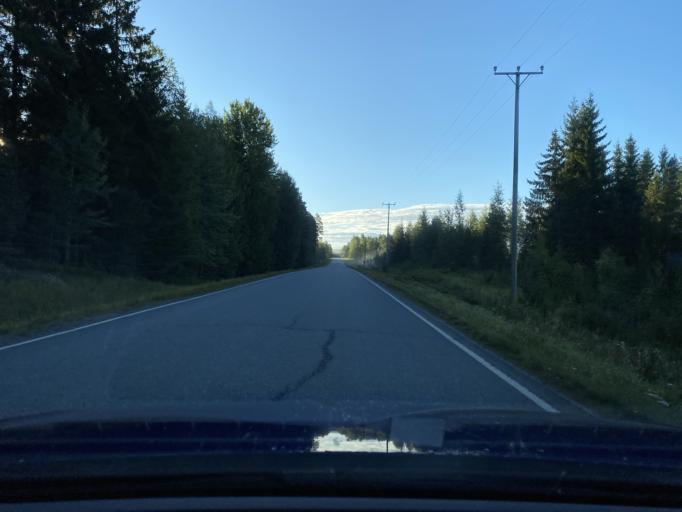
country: FI
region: Haeme
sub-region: Forssa
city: Tammela
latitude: 60.9237
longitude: 23.8186
